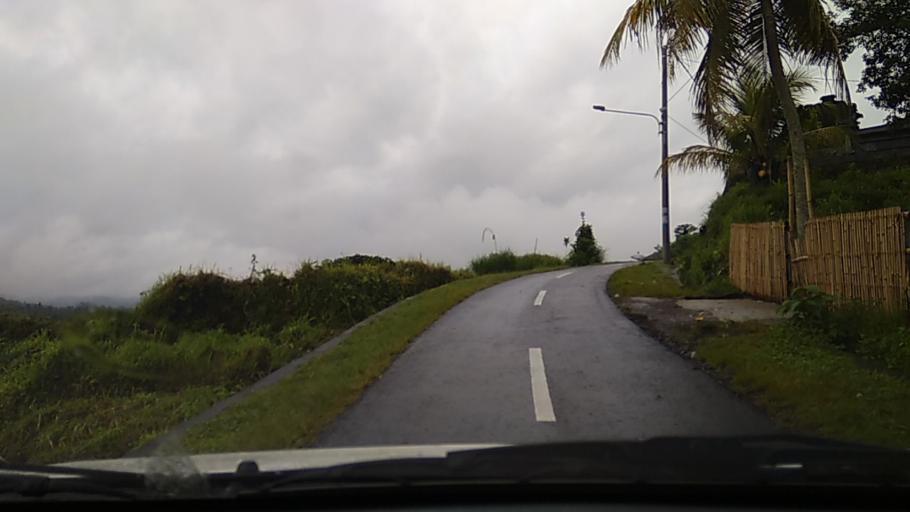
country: ID
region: Bali
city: Tiyingtali Kelod
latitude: -8.4014
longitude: 115.6171
